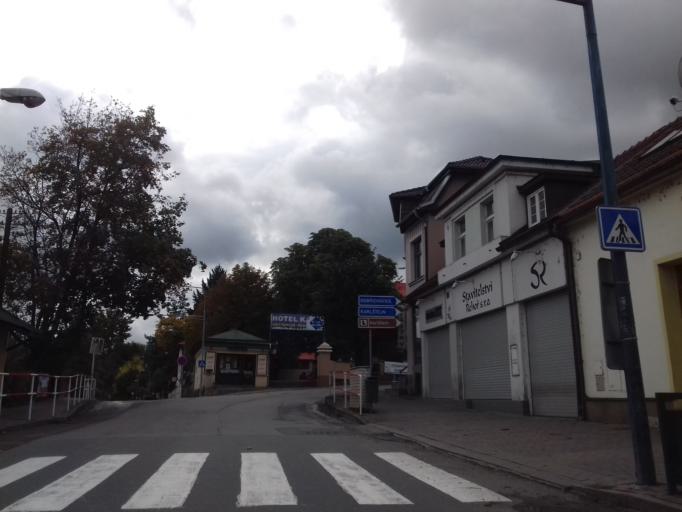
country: CZ
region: Central Bohemia
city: Cernosice
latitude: 49.9590
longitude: 14.3232
